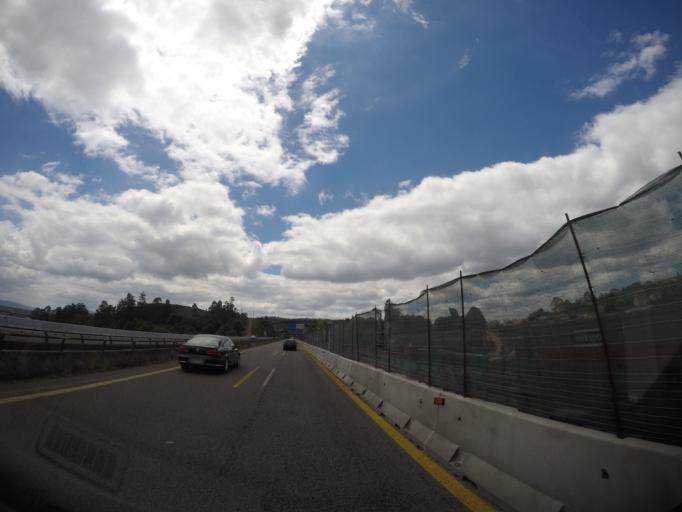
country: ES
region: Galicia
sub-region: Provincia da Coruna
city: Rois
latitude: 42.8139
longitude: -8.7662
